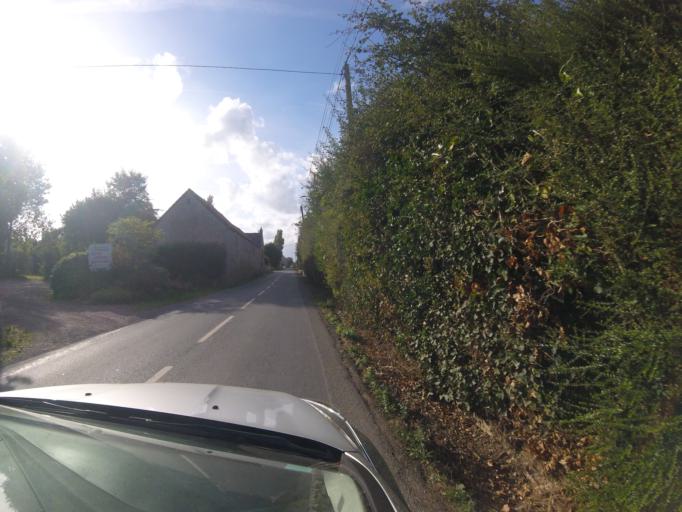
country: FR
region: Lower Normandy
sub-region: Departement du Calvados
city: Port-en-Bessin-Huppain
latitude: 49.3495
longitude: -0.8216
